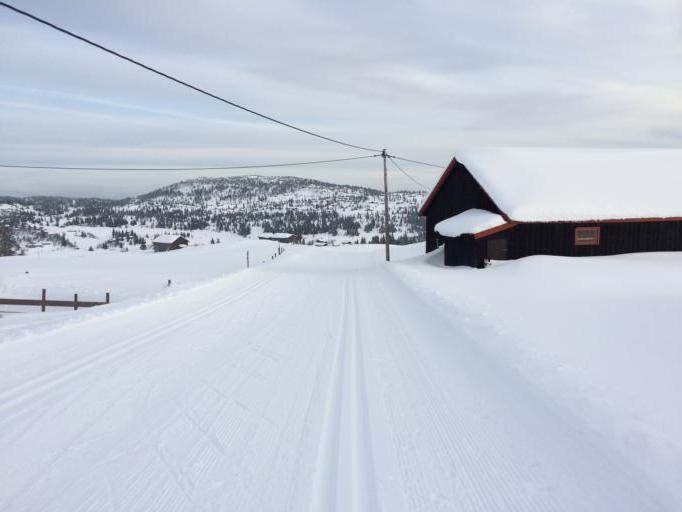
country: NO
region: Oppland
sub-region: Gausdal
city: Segalstad bru
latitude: 61.3151
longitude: 10.0512
